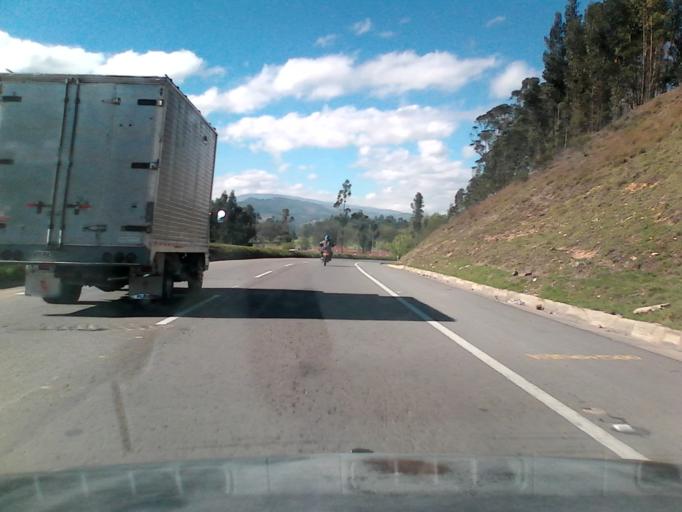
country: CO
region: Boyaca
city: Duitama
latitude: 5.7957
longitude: -73.0437
